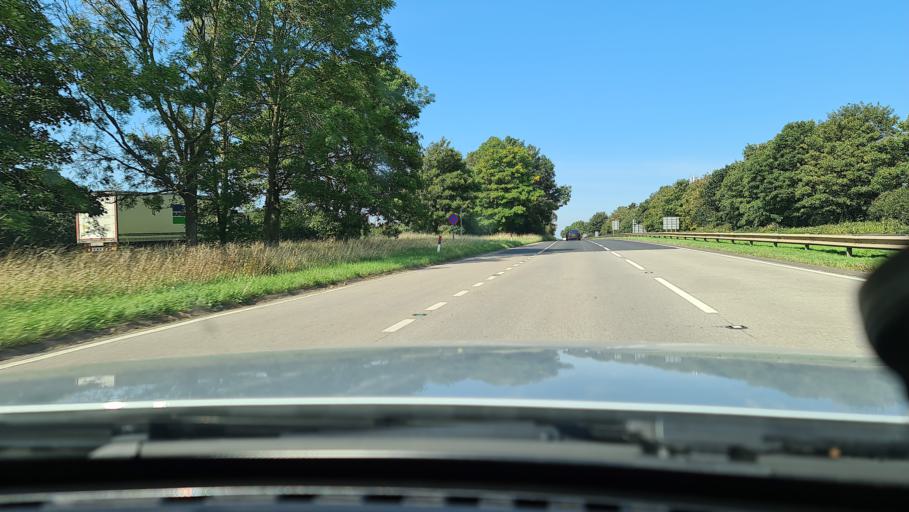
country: GB
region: England
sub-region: Leicestershire
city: Sapcote
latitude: 52.4937
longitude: -1.3056
